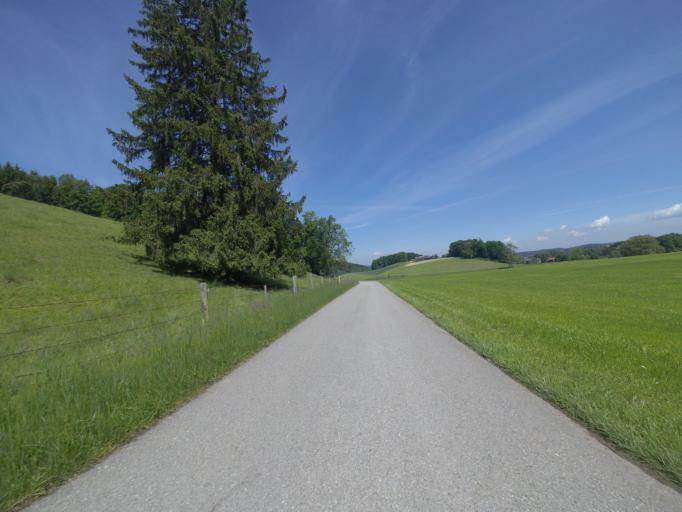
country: DE
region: Bavaria
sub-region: Upper Bavaria
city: Petting
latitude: 47.9114
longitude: 12.7964
